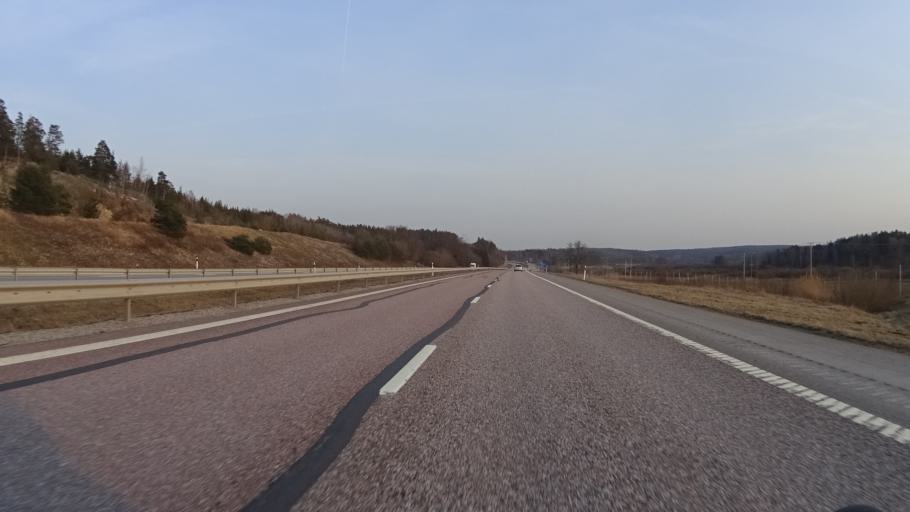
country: SE
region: Soedermanland
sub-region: Strangnas Kommun
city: Akers Styckebruk
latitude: 59.2612
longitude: 17.1450
